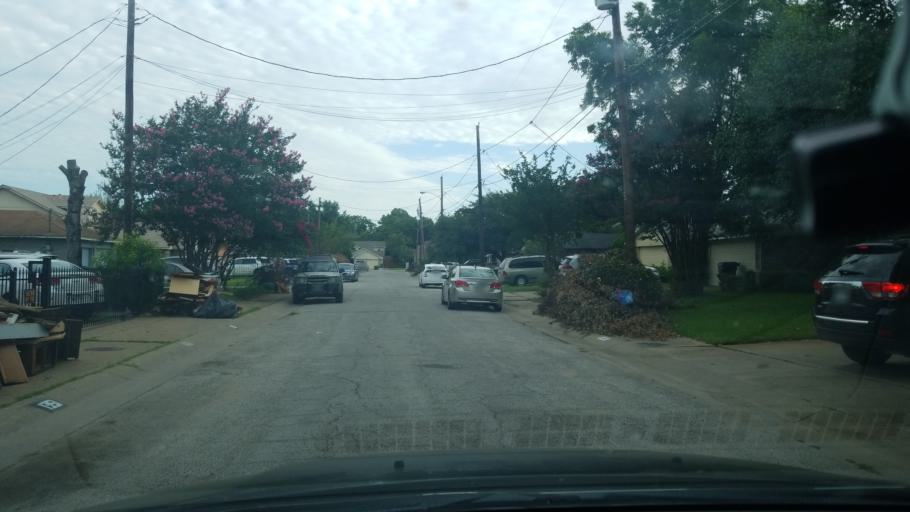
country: US
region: Texas
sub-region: Dallas County
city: Balch Springs
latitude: 32.7357
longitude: -96.6603
